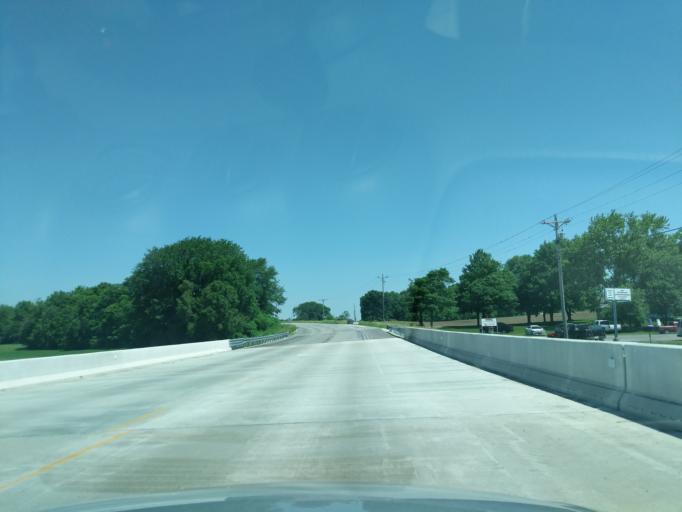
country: US
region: Indiana
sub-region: Whitley County
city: Columbia City
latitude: 41.1146
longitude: -85.4715
